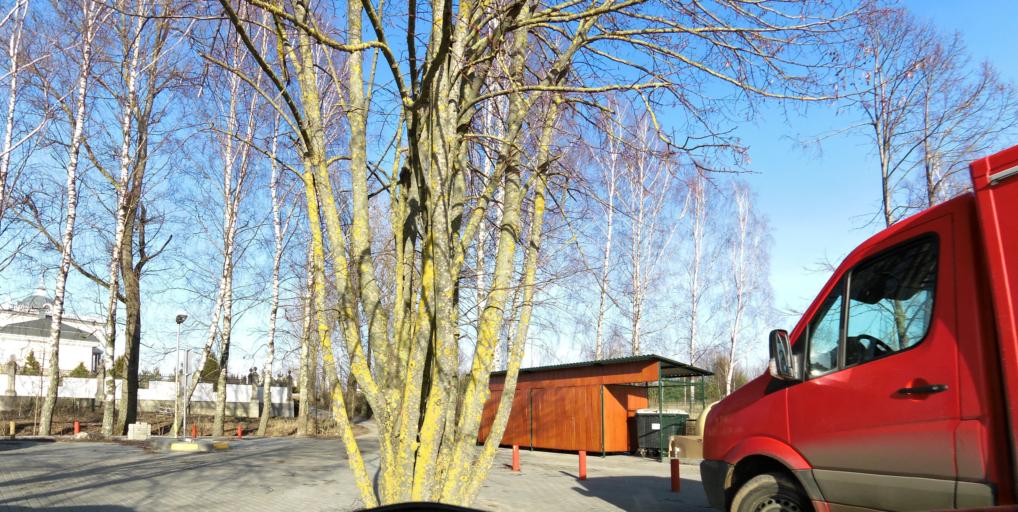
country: LT
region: Vilnius County
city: Pilaite
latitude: 54.7065
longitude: 25.1601
